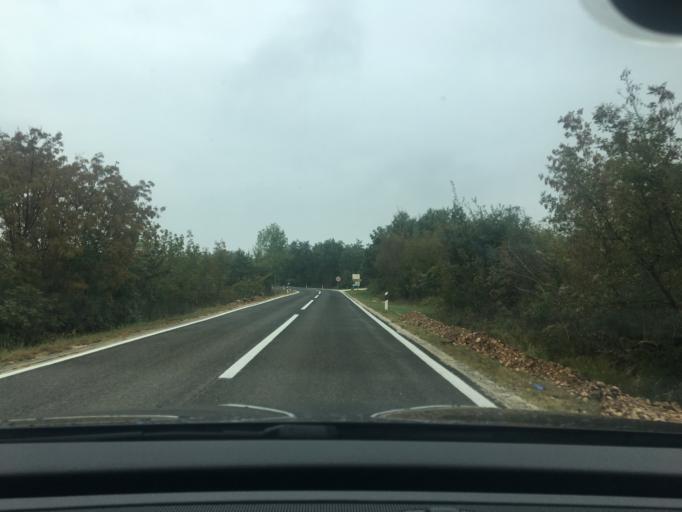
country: HR
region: Istarska
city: Buje
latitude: 45.4260
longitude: 13.6589
